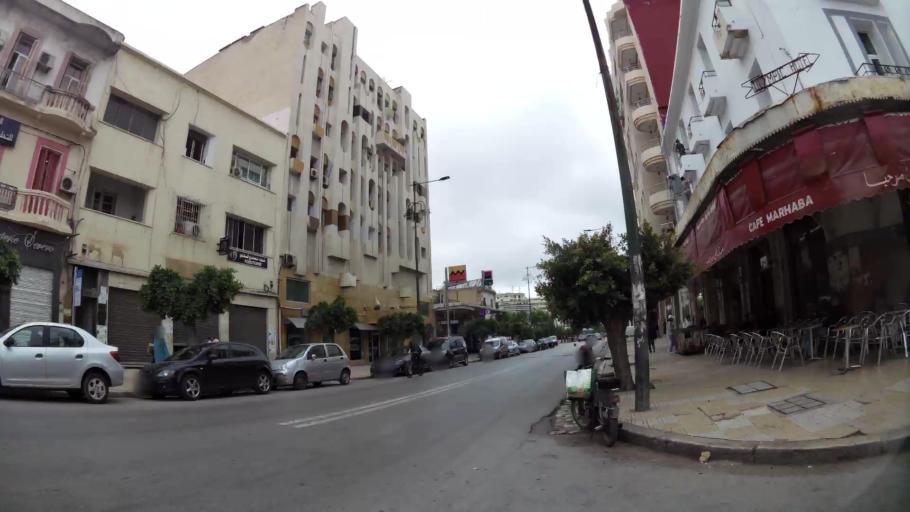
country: MA
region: Fes-Boulemane
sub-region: Fes
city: Fes
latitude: 34.0396
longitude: -4.9988
